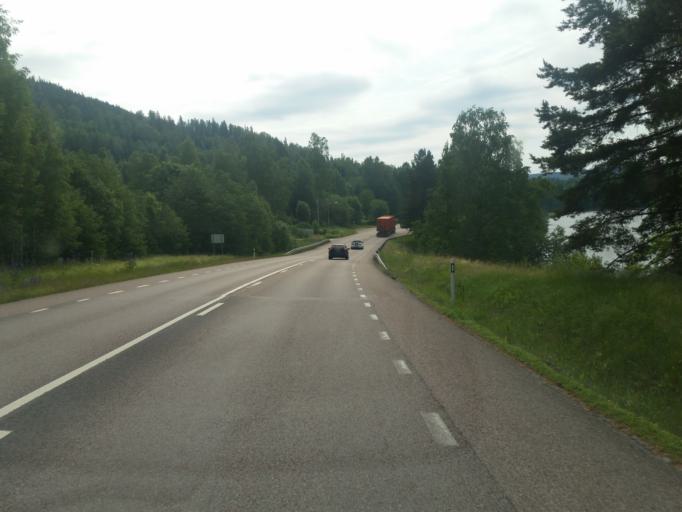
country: SE
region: Dalarna
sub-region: Gagnefs Kommun
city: Djuras
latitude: 60.5464
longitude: 15.2765
